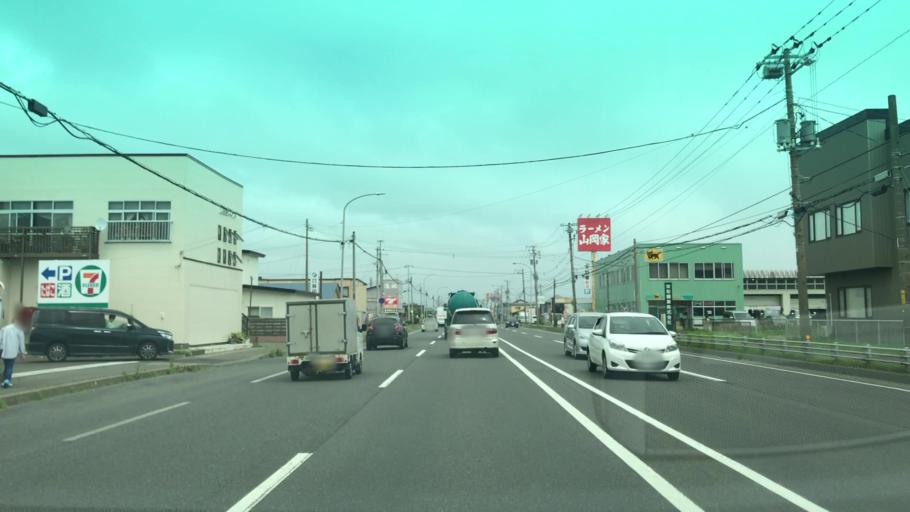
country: JP
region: Hokkaido
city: Muroran
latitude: 42.3624
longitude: 141.0556
